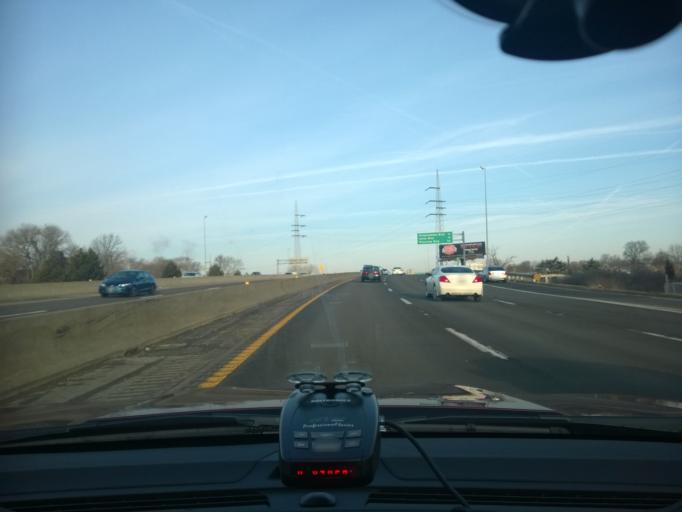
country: US
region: Missouri
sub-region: Saint Louis County
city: Pine Lawn
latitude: 38.6836
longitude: -90.2403
